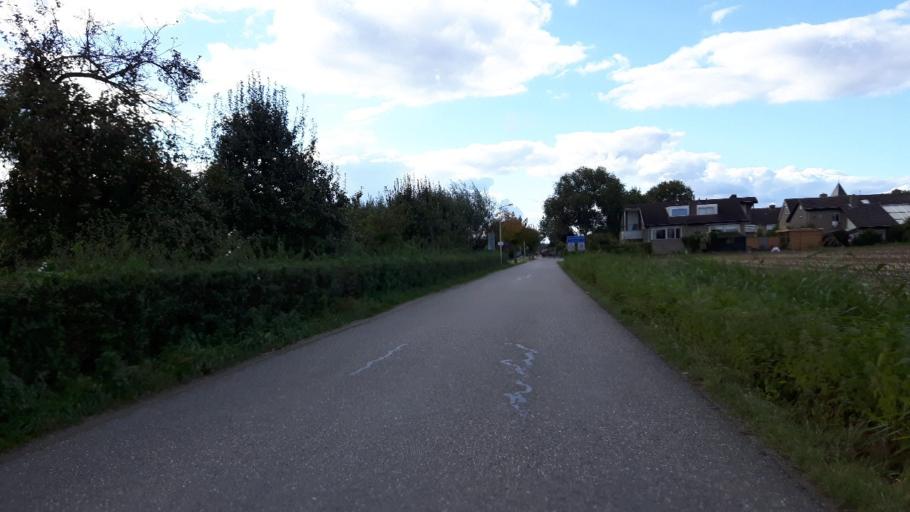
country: NL
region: South Holland
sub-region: Gemeente Leerdam
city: Leerdam
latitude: 51.9182
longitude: 5.1213
